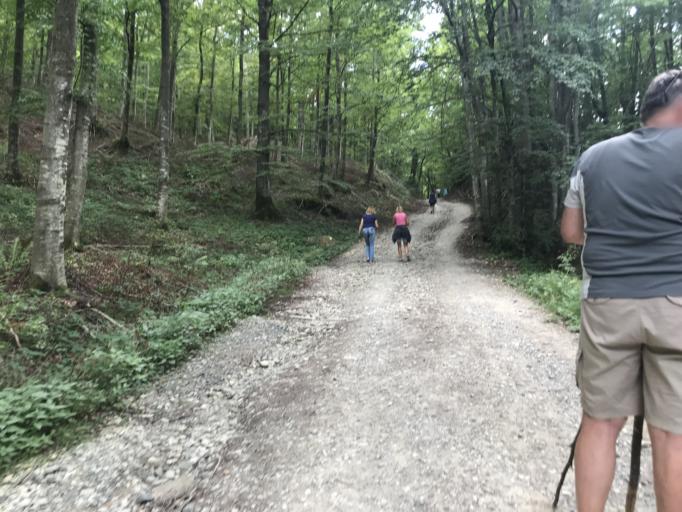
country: IT
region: Emilia-Romagna
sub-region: Provincia di Bologna
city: San Benedetto Val di Sambro
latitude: 44.1594
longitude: 11.2624
